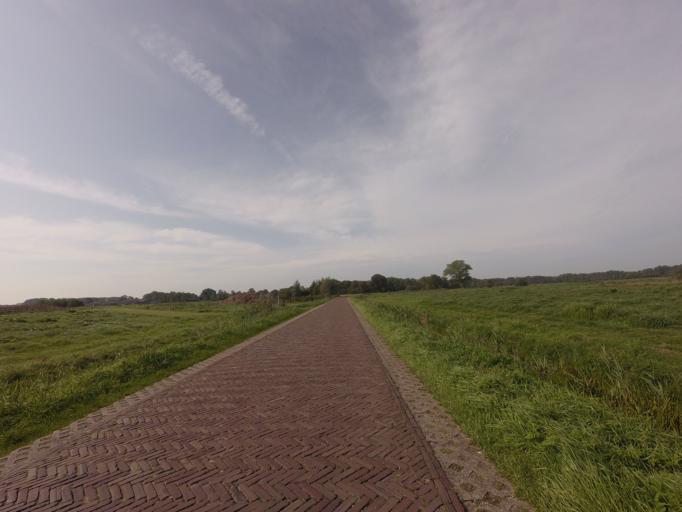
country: NL
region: Groningen
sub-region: Gemeente Leek
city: Leek
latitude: 53.1716
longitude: 6.4136
